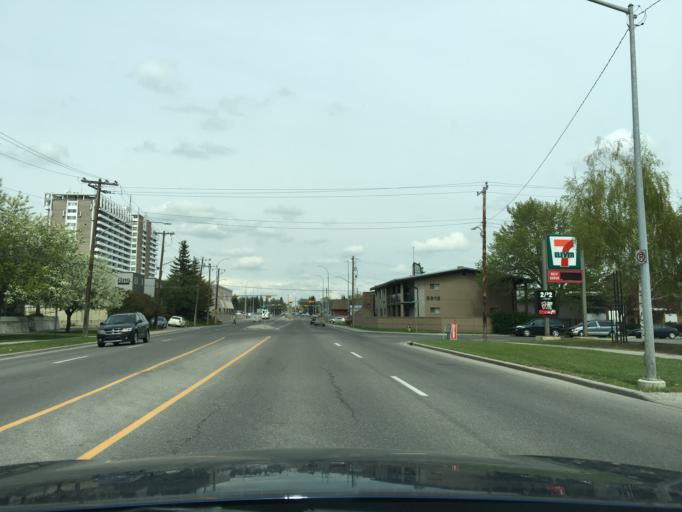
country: CA
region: Alberta
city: Calgary
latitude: 50.9910
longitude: -114.0831
